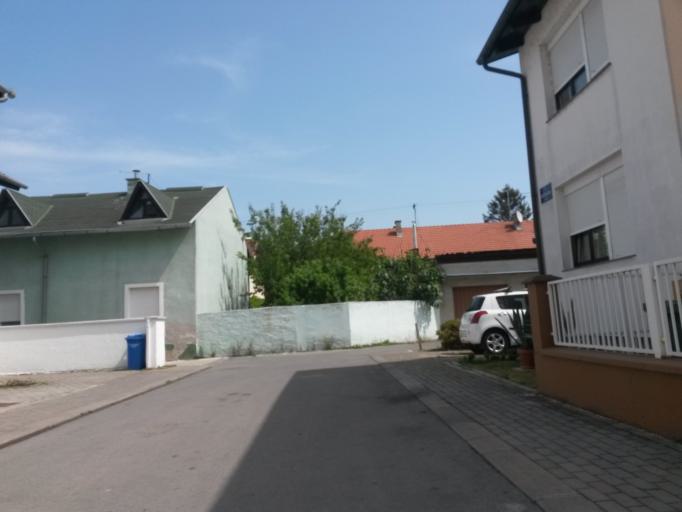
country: HR
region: Osjecko-Baranjska
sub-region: Grad Osijek
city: Osijek
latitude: 45.5460
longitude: 18.6727
